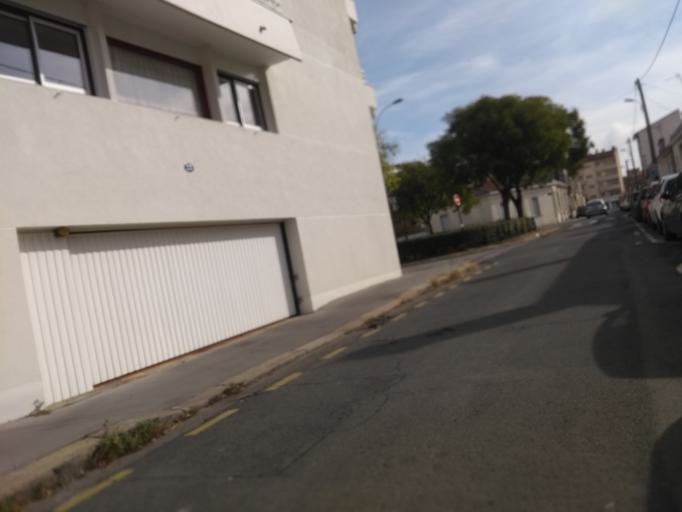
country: FR
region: Aquitaine
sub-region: Departement de la Gironde
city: Talence
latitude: 44.8229
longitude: -0.5955
